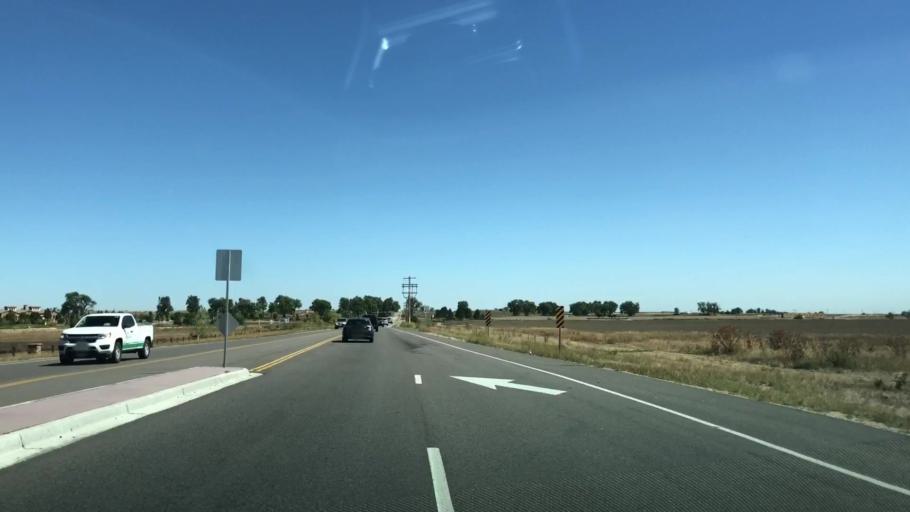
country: US
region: Colorado
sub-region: Weld County
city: Windsor
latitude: 40.5228
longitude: -104.9621
